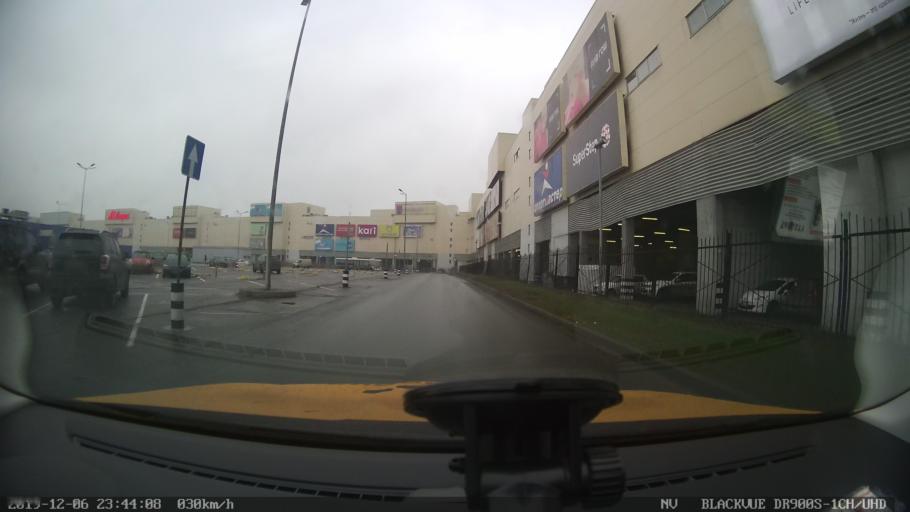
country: RU
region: Moscow
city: Rostokino
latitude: 55.8450
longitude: 37.6655
